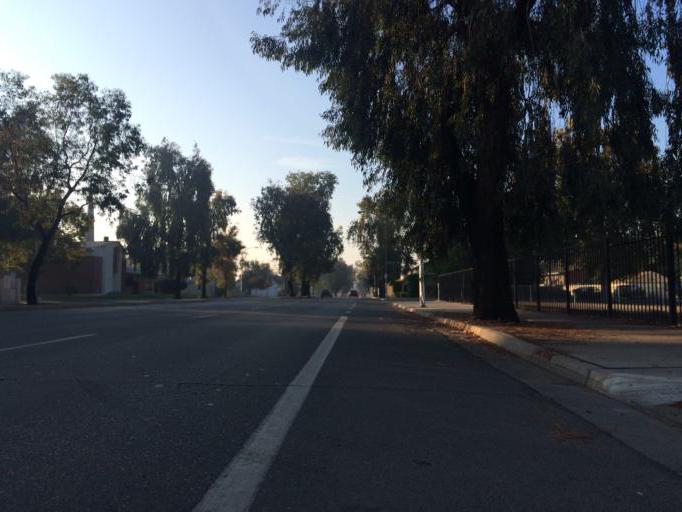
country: US
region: California
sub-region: Fresno County
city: Fresno
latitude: 36.7492
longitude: -119.7726
